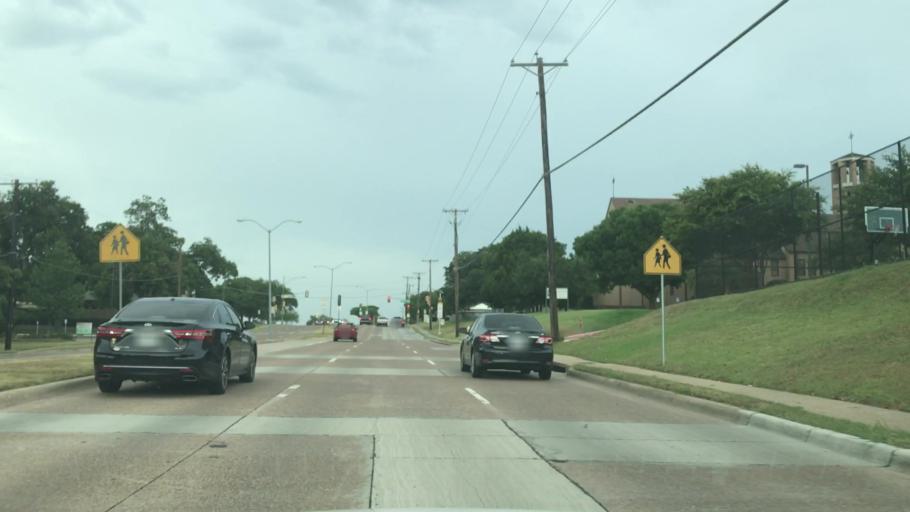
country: US
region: Texas
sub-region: Dallas County
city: Richardson
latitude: 32.8789
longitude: -96.7104
